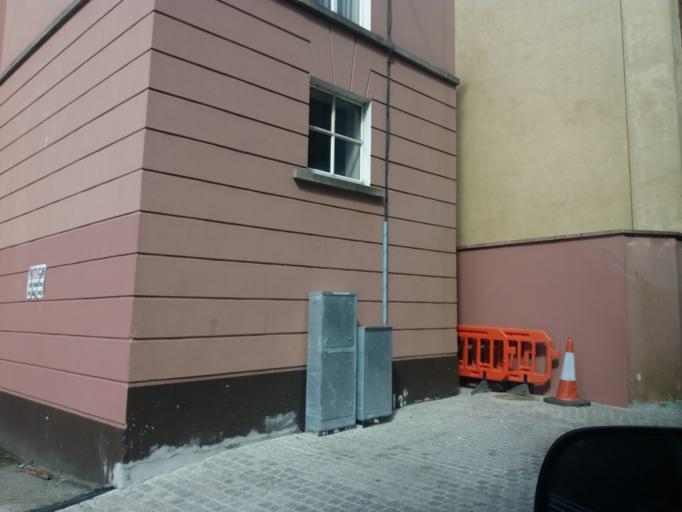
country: IE
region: Munster
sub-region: Waterford
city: Waterford
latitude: 52.2596
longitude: -7.1099
